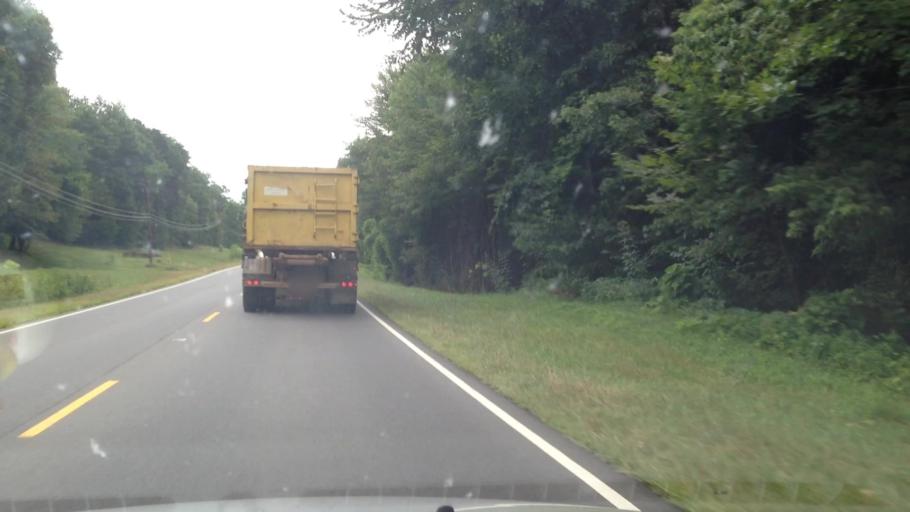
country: US
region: North Carolina
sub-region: Rockingham County
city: Reidsville
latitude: 36.3663
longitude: -79.7140
